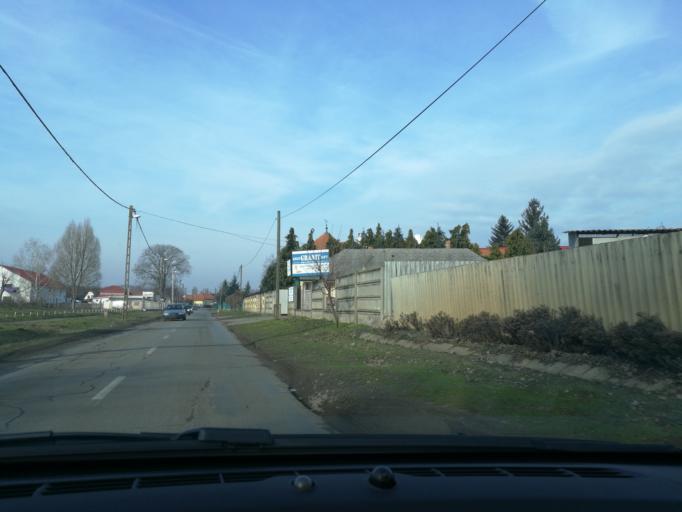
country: HU
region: Szabolcs-Szatmar-Bereg
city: Nyiregyhaza
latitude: 47.9638
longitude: 21.7342
